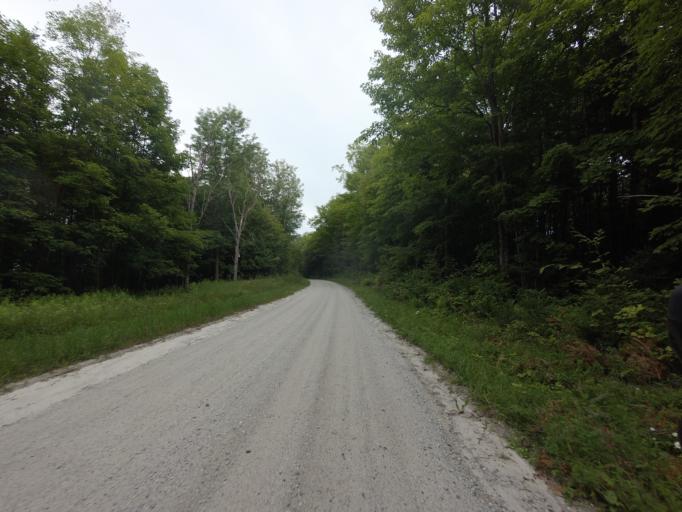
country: CA
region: Ontario
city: Perth
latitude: 44.8528
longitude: -76.5695
